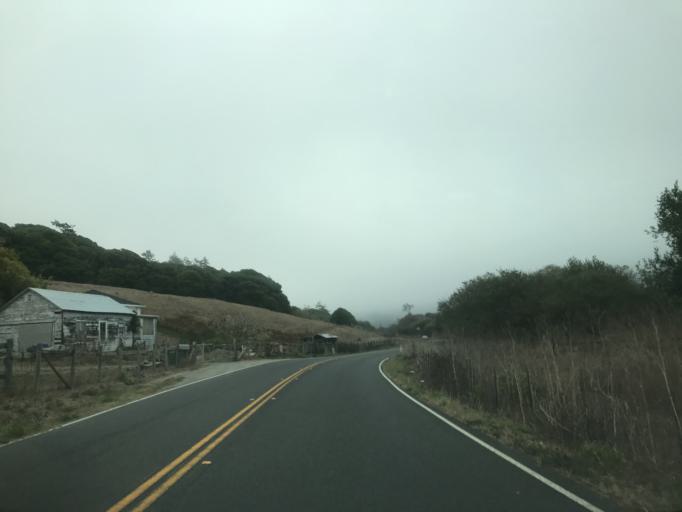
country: US
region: California
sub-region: Sonoma County
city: Monte Rio
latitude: 38.4485
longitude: -123.0880
